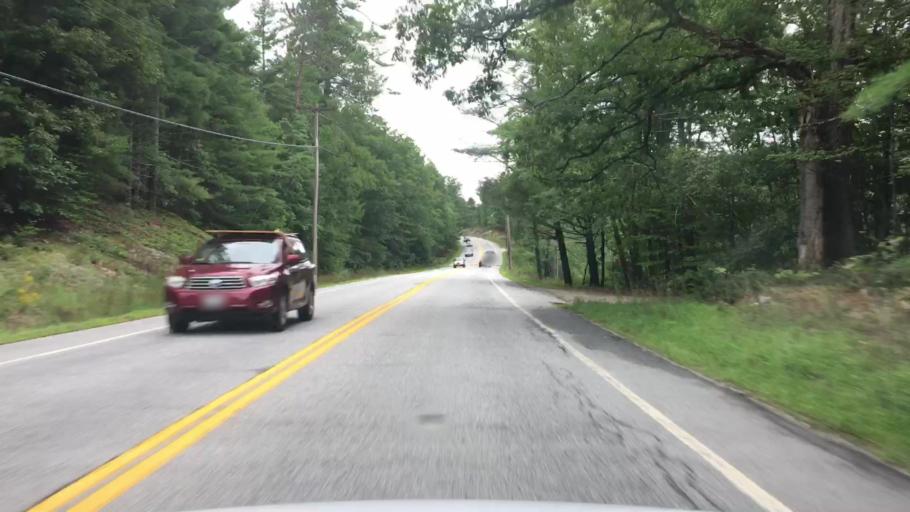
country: US
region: Maine
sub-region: Oxford County
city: Hiram
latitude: 43.8578
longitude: -70.7900
